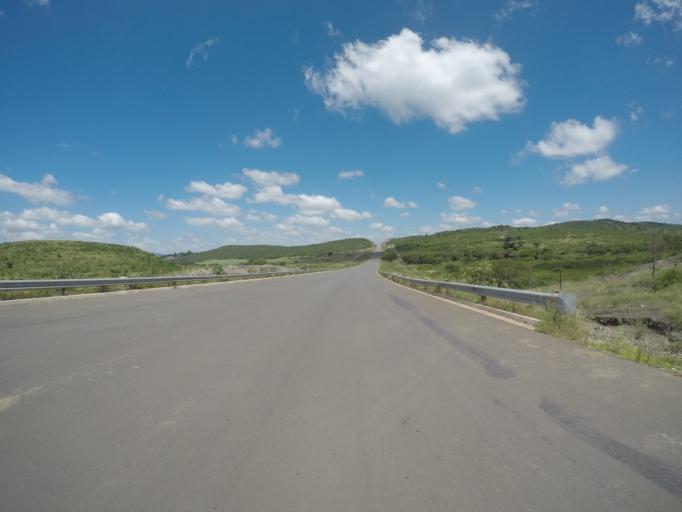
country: ZA
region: KwaZulu-Natal
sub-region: uThungulu District Municipality
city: Empangeni
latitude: -28.6164
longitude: 31.7550
